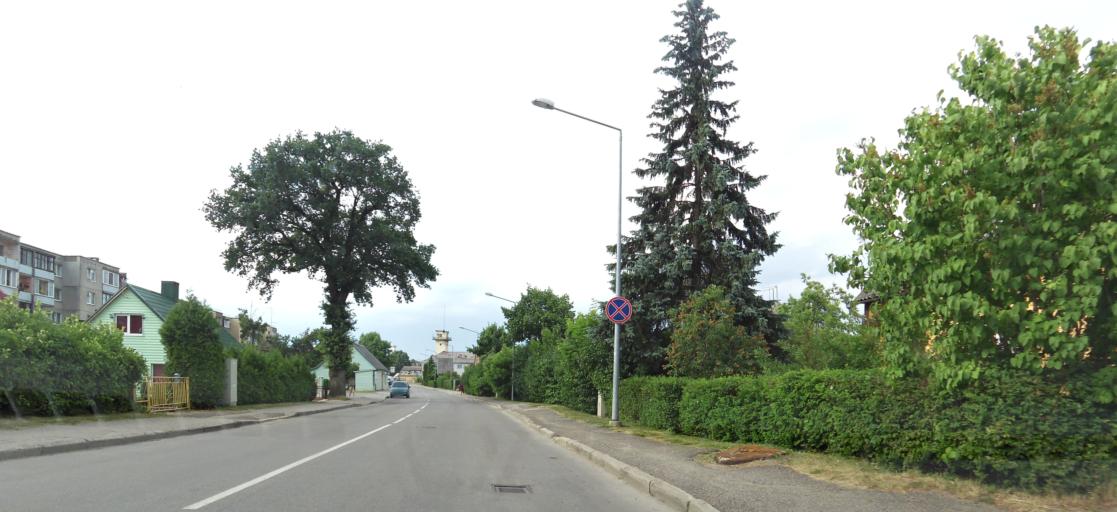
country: LT
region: Panevezys
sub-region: Birzai
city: Birzai
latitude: 56.1989
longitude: 24.7585
